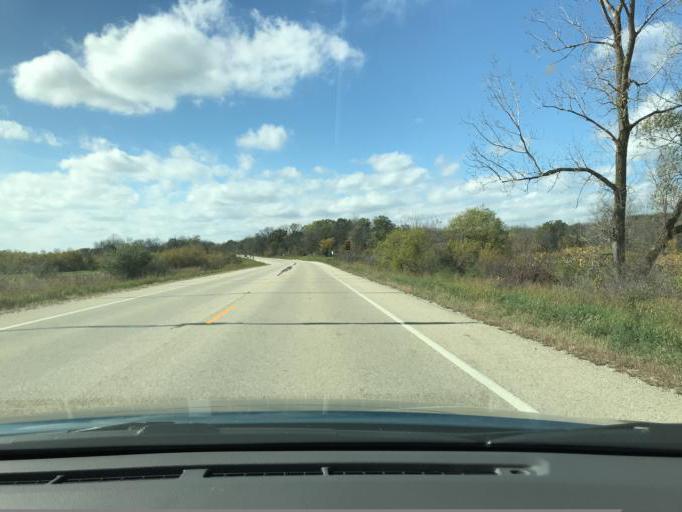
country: US
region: Wisconsin
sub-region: Racine County
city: Eagle Lake
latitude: 42.6370
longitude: -88.1559
